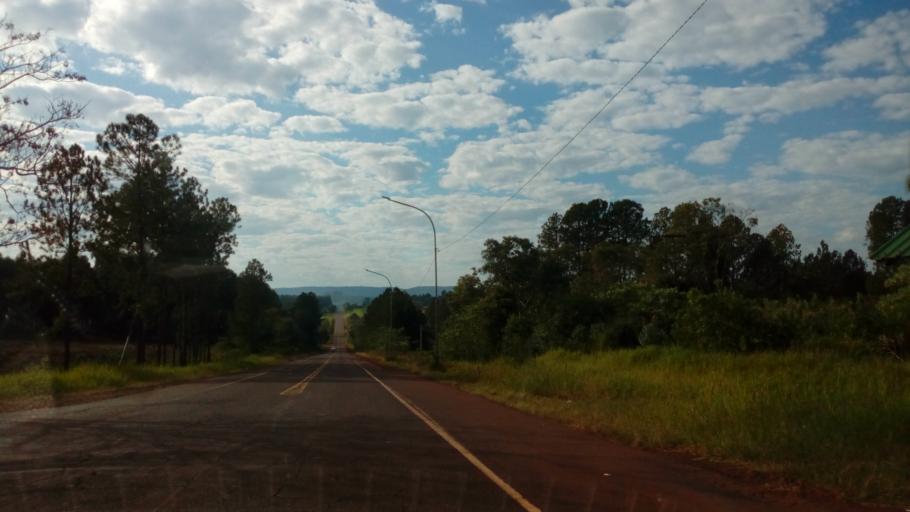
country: AR
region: Misiones
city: Ruiz de Montoya
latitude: -27.0591
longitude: -55.0405
